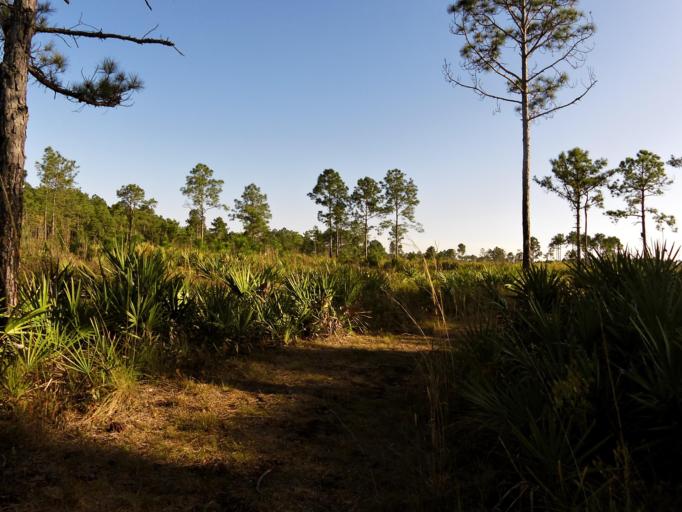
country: US
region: Florida
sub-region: Duval County
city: Atlantic Beach
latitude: 30.4758
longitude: -81.4885
